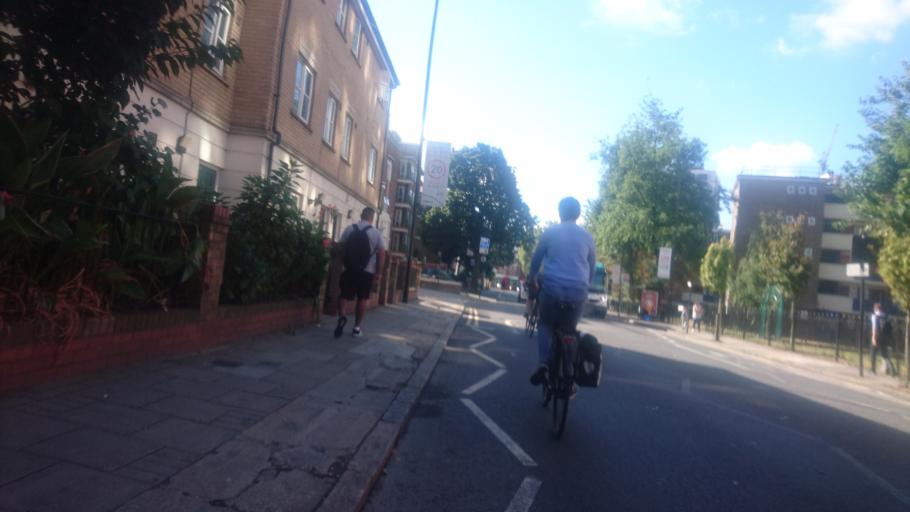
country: GB
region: England
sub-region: Greater London
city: Barbican
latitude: 51.5331
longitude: -0.0875
